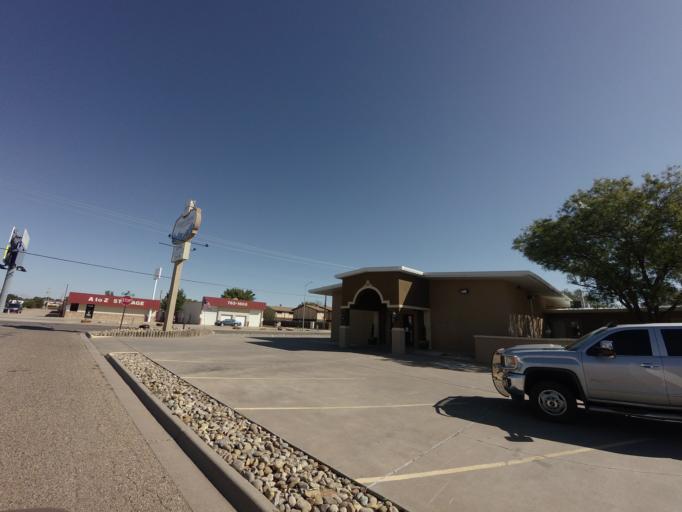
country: US
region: New Mexico
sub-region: Curry County
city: Clovis
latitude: 34.4335
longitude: -103.1940
